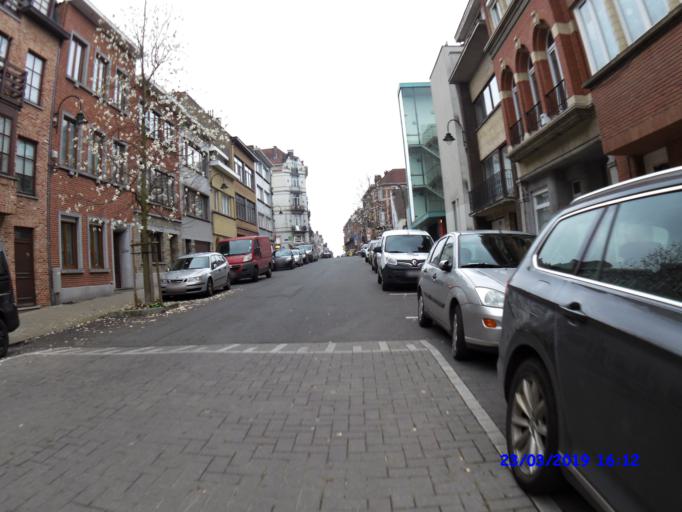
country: BE
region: Brussels Capital
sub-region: Bruxelles-Capitale
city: Brussels
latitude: 50.8771
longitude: 4.3380
